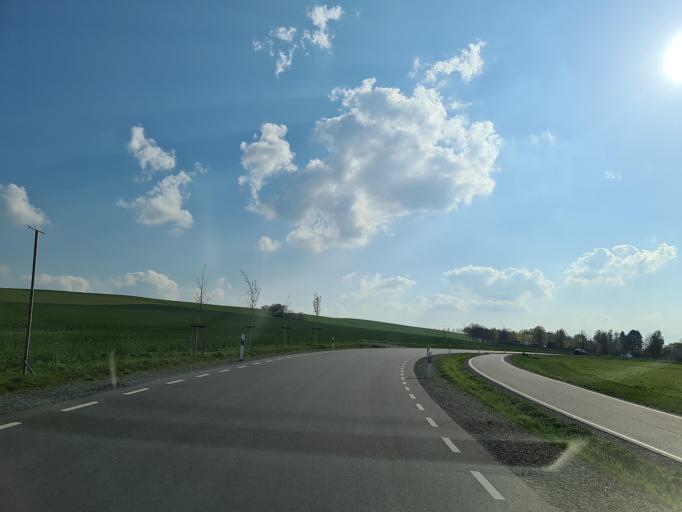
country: DE
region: Saxony
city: Jahnsdorf
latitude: 50.7526
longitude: 12.8704
